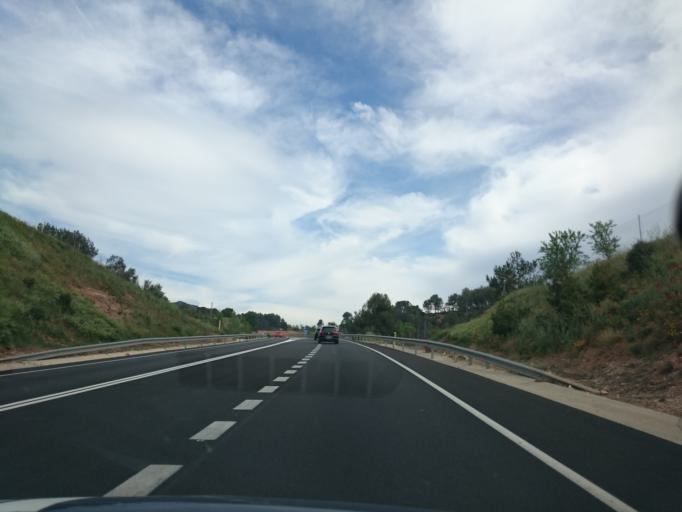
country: ES
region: Catalonia
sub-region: Provincia de Barcelona
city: Sant Salvador de Guardiola
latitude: 41.6774
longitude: 1.7547
